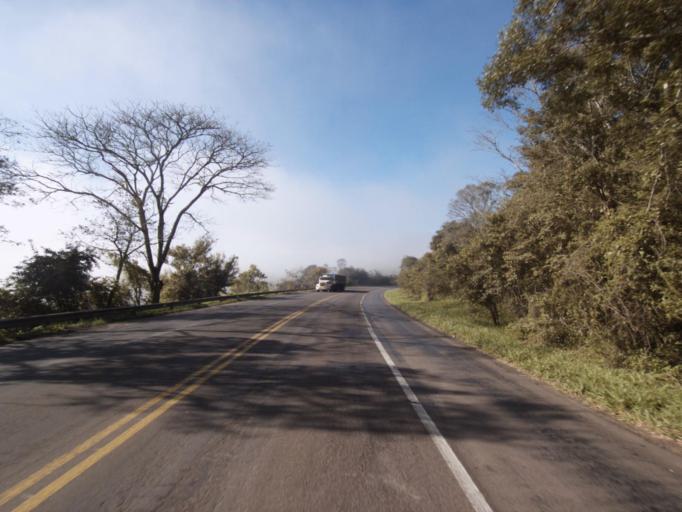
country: BR
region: Rio Grande do Sul
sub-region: Frederico Westphalen
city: Frederico Westphalen
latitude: -26.8217
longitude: -53.4242
